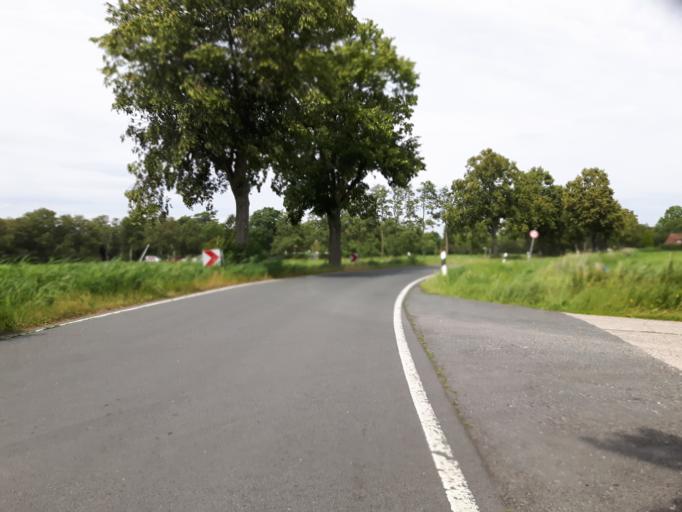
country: DE
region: Lower Saxony
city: Rastede
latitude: 53.3393
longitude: 8.2441
